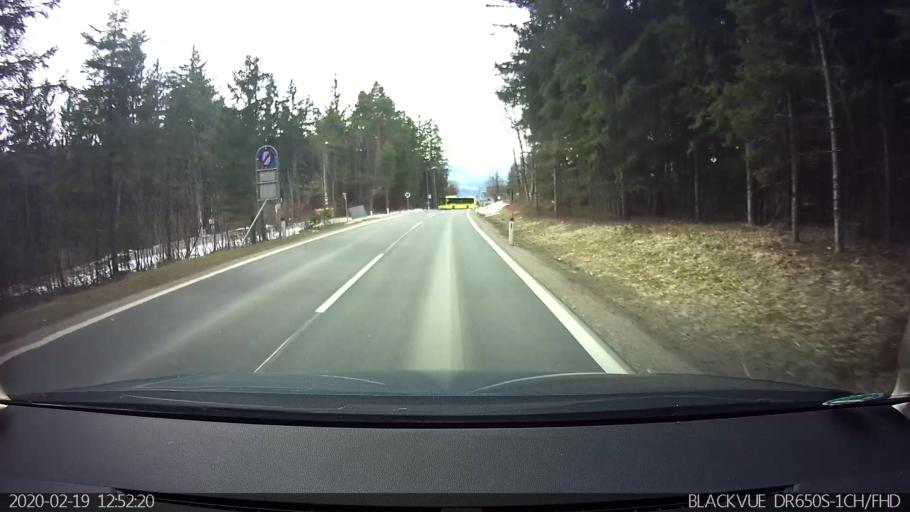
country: AT
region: Tyrol
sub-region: Politischer Bezirk Innsbruck Land
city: Absam
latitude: 47.3082
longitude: 11.5232
